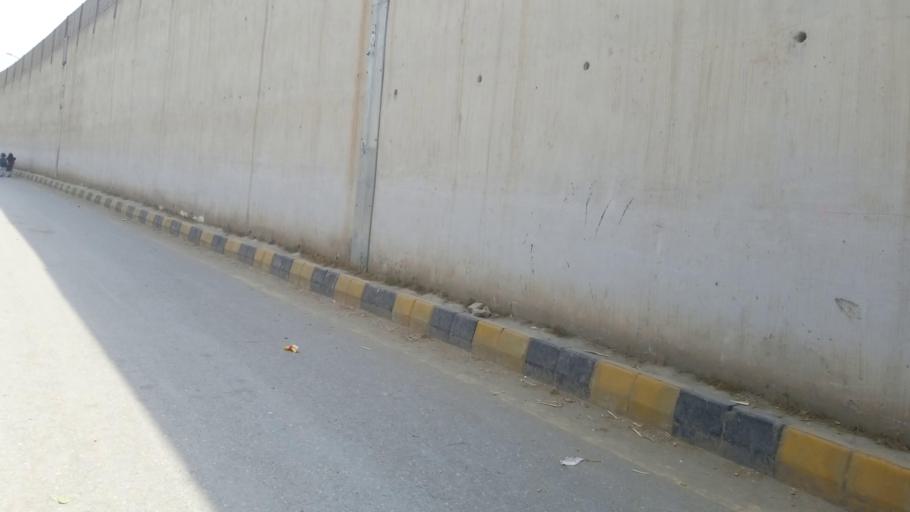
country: PK
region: Khyber Pakhtunkhwa
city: Peshawar
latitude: 34.0300
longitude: 71.5472
